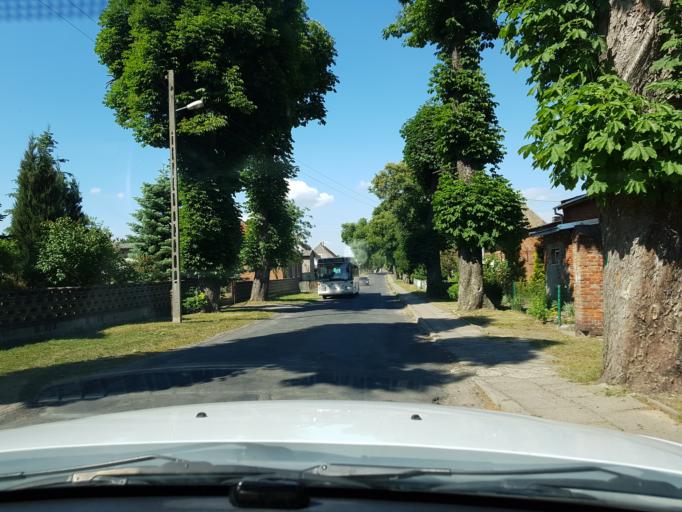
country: PL
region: West Pomeranian Voivodeship
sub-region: Powiat gryfinski
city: Gryfino
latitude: 53.1700
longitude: 14.5406
